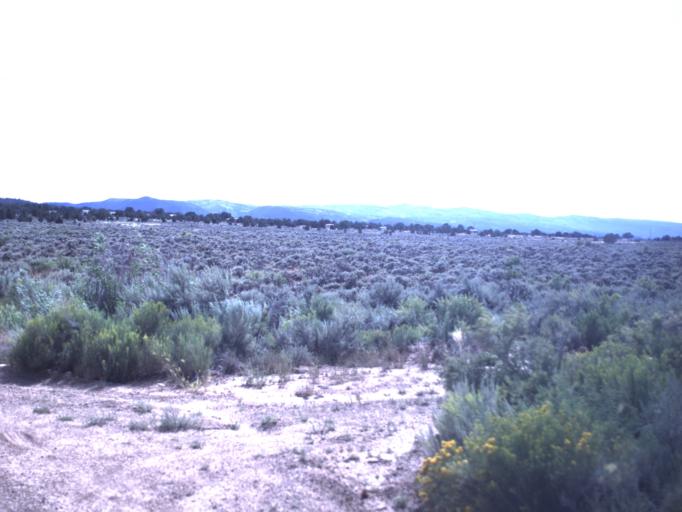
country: US
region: Utah
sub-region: Duchesne County
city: Duchesne
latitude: 40.2057
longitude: -110.7314
